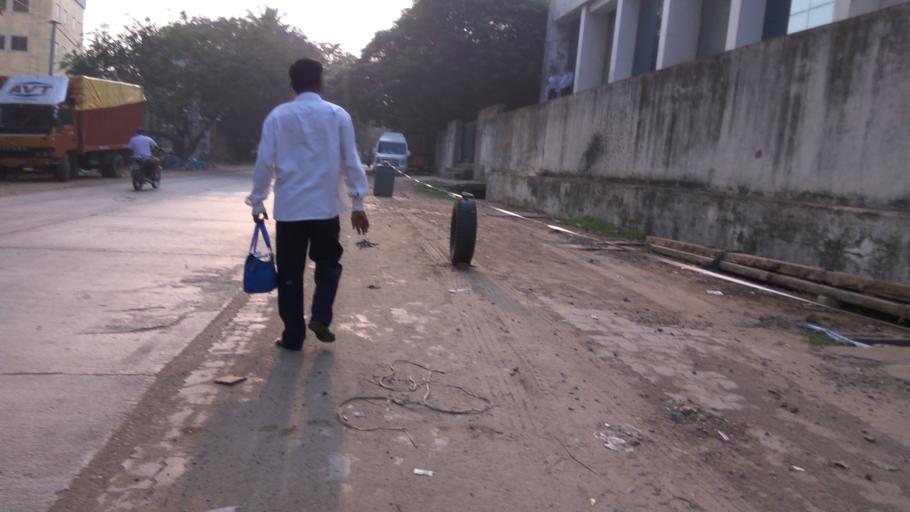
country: IN
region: Tamil Nadu
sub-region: Kancheepuram
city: Alandur
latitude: 13.0130
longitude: 80.2110
